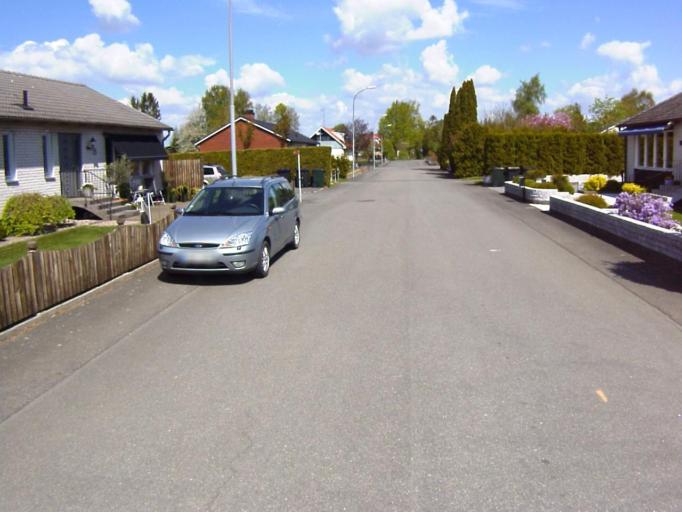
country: SE
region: Skane
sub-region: Kristianstads Kommun
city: Fjalkinge
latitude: 56.0139
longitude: 14.2297
